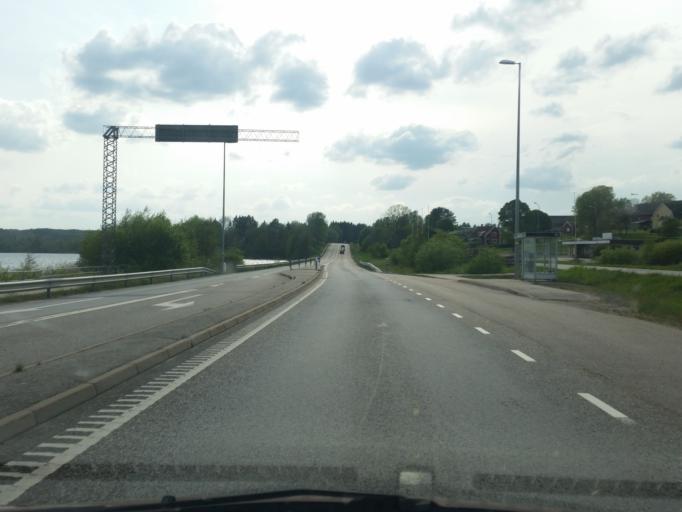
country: SE
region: Vaestra Goetaland
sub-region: Ulricehamns Kommun
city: Ulricehamn
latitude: 57.8088
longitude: 13.2560
